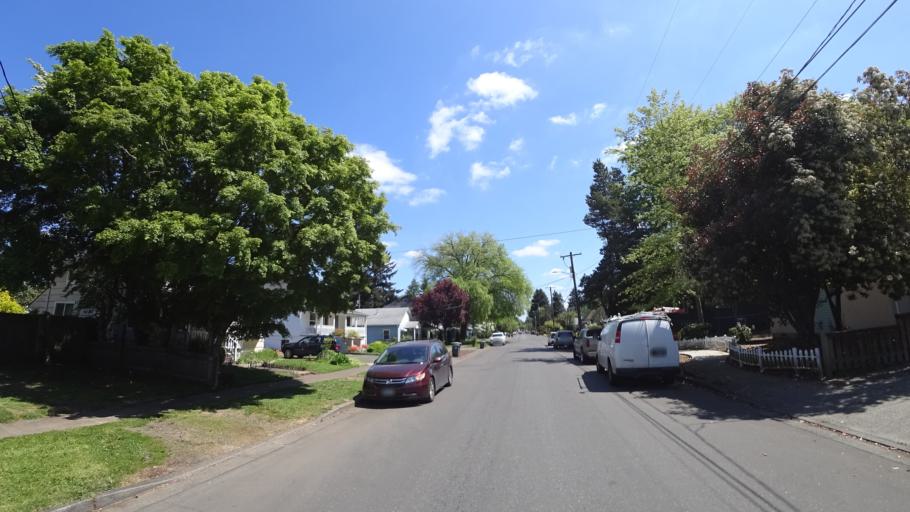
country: US
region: Oregon
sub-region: Washington County
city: Hillsboro
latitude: 45.5162
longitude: -122.9819
